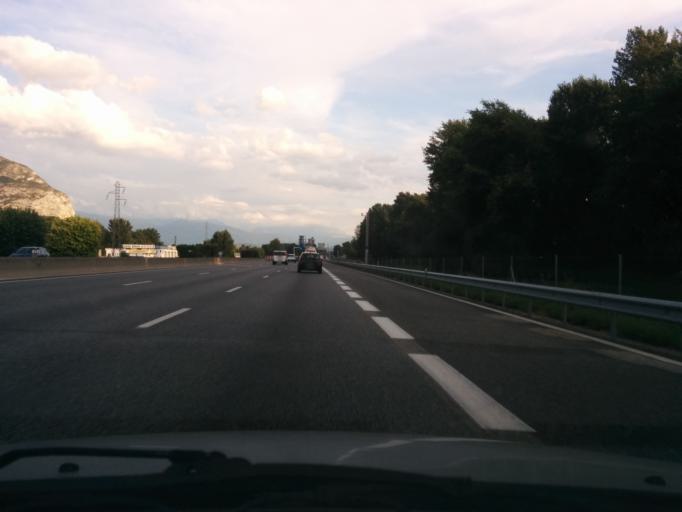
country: FR
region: Rhone-Alpes
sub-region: Departement de l'Isere
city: Fontanil-Cornillon
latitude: 45.2428
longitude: 5.6580
